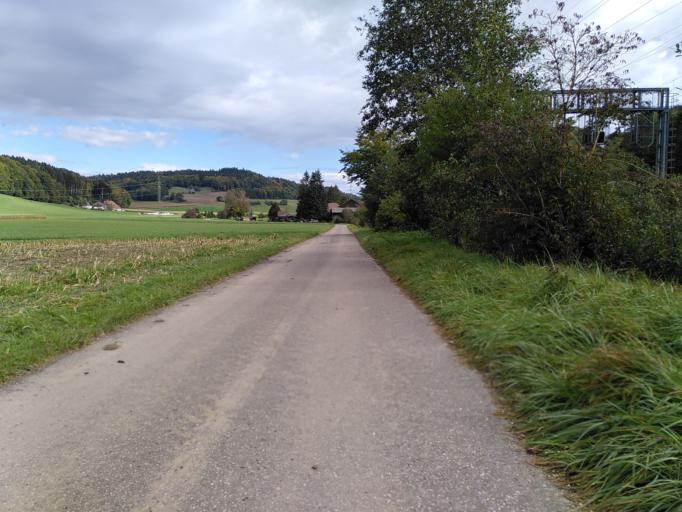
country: CH
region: Bern
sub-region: Emmental District
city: Wynigen
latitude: 47.1220
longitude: 7.6725
